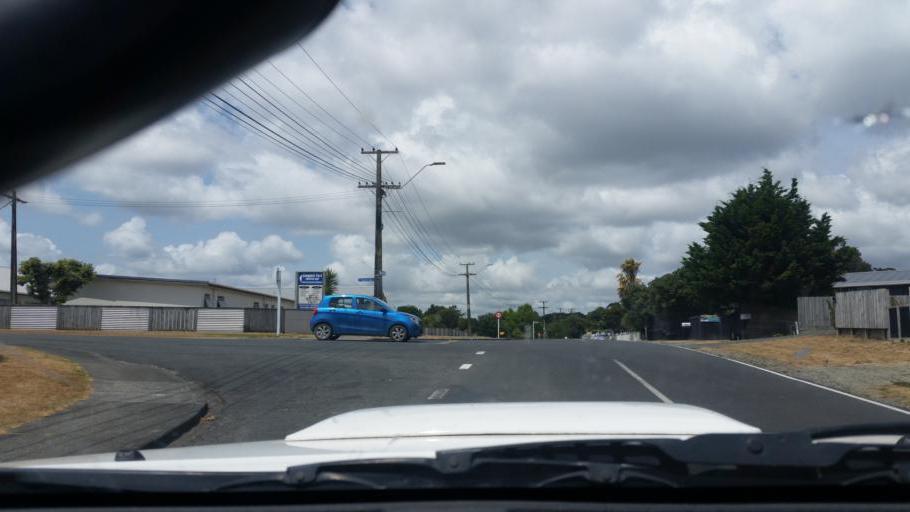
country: NZ
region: Auckland
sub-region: Auckland
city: Wellsford
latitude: -36.0910
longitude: 174.5845
